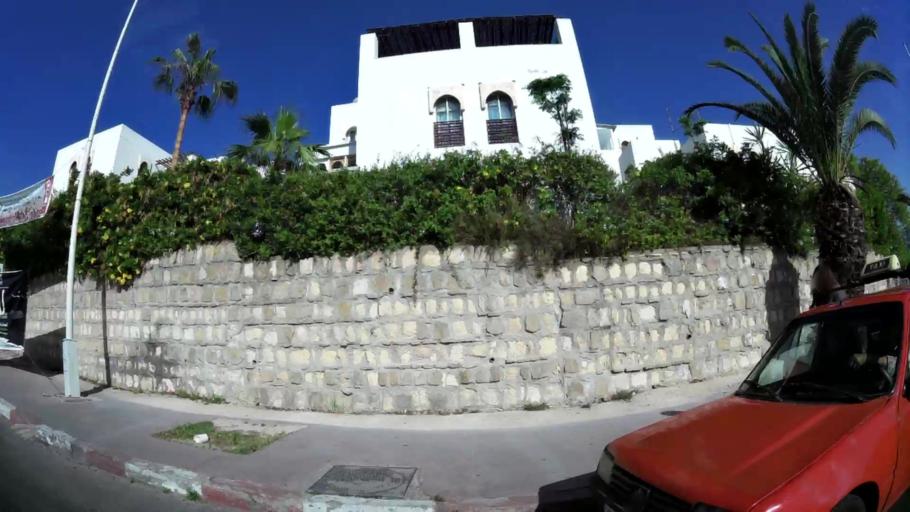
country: MA
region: Souss-Massa-Draa
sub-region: Agadir-Ida-ou-Tnan
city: Agadir
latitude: 30.4276
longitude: -9.5923
